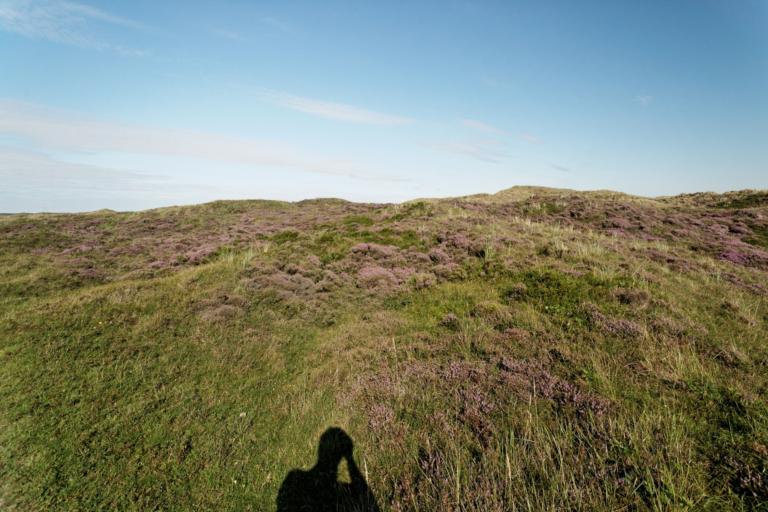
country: NL
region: North Holland
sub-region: Gemeente Texel
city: Den Burg
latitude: 53.0287
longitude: 4.7267
